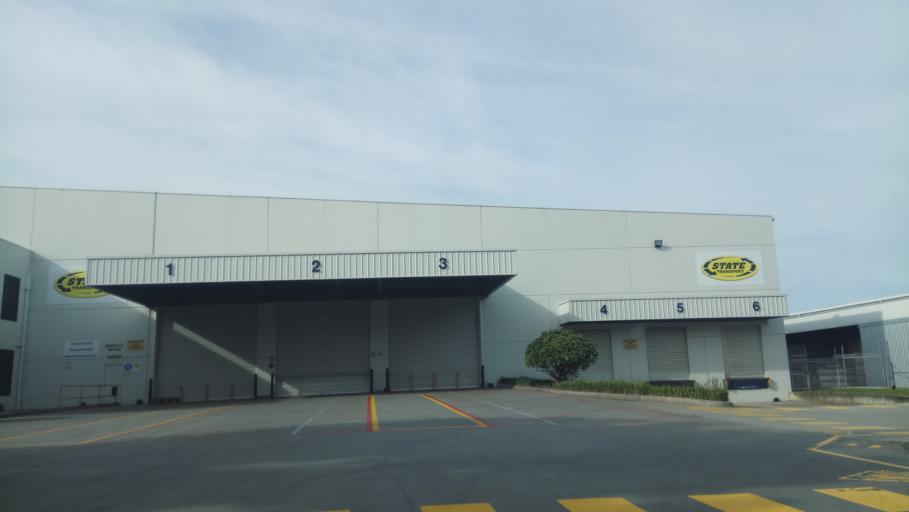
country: AU
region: Victoria
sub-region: Monash
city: Oakleigh South
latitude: -37.9451
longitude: 145.0821
